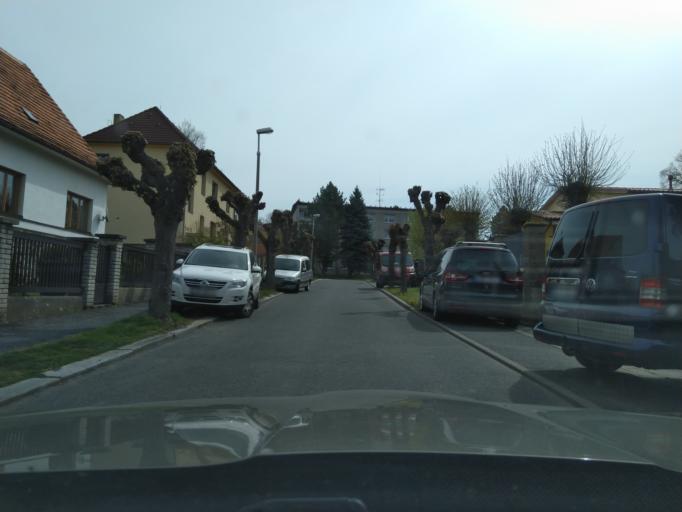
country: CZ
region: Plzensky
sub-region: Okres Klatovy
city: Susice
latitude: 49.2299
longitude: 13.5242
